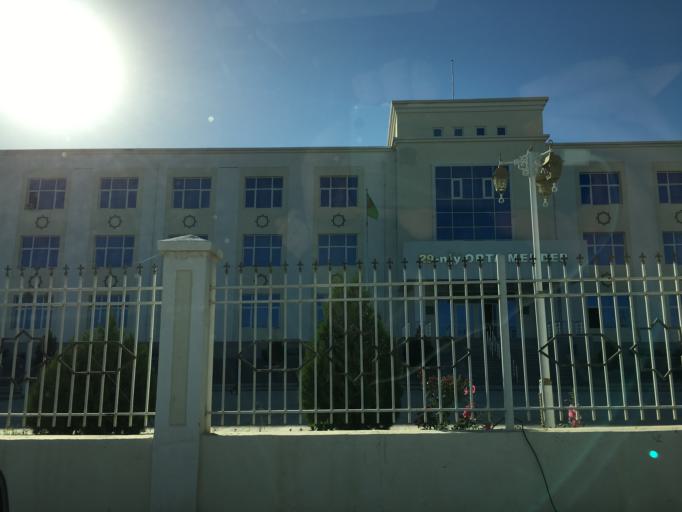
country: TM
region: Ahal
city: Baharly
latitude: 38.3731
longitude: 57.4972
